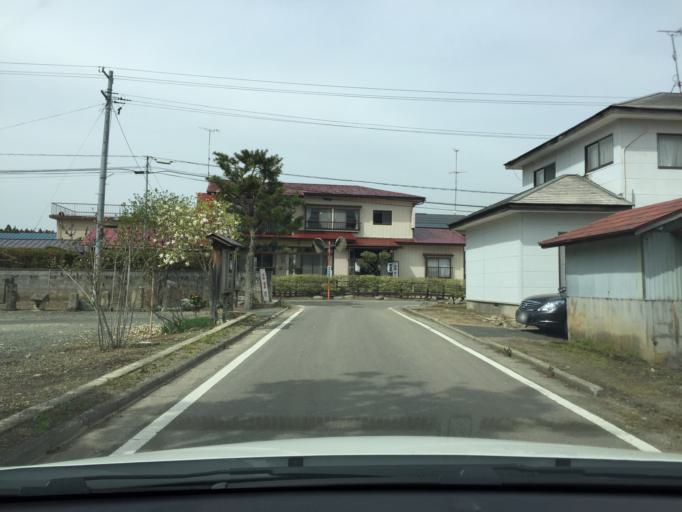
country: JP
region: Fukushima
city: Inawashiro
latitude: 37.5164
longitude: 140.1332
